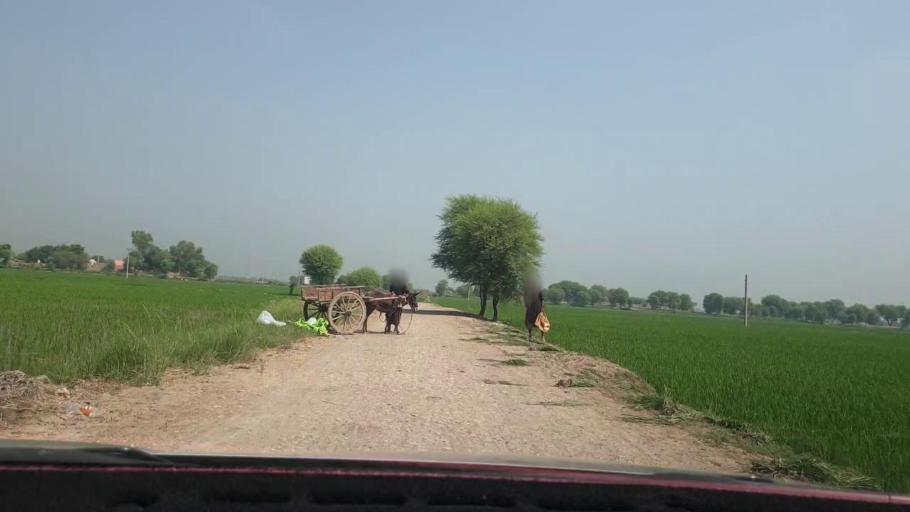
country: PK
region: Sindh
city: Warah
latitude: 27.4316
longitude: 67.8559
